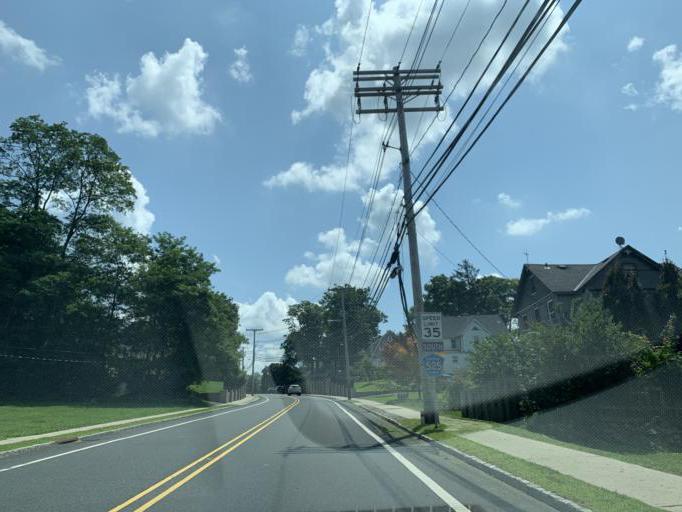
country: US
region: New Jersey
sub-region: Somerset County
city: Bernardsville
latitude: 40.7165
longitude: -74.5685
